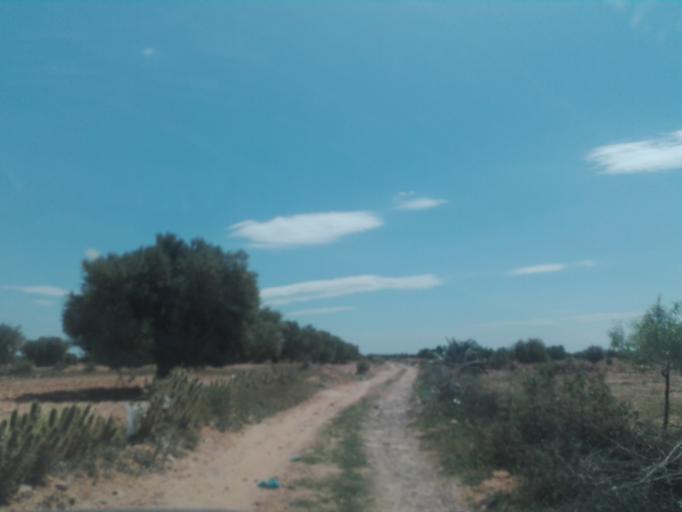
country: TN
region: Safaqis
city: Sfax
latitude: 34.6542
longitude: 10.5878
